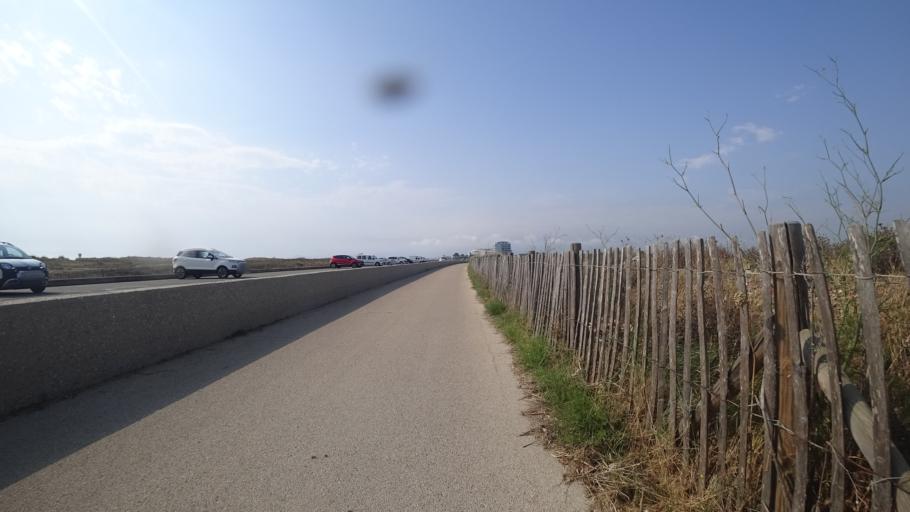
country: FR
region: Languedoc-Roussillon
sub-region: Departement des Pyrenees-Orientales
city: Saint-Cyprien-Plage
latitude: 42.6451
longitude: 3.0336
